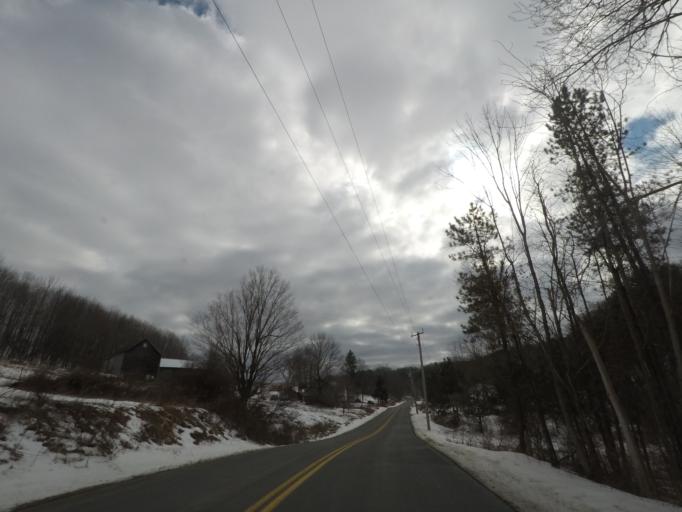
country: US
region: New York
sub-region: Rensselaer County
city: Hoosick Falls
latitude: 42.8874
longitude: -73.4184
